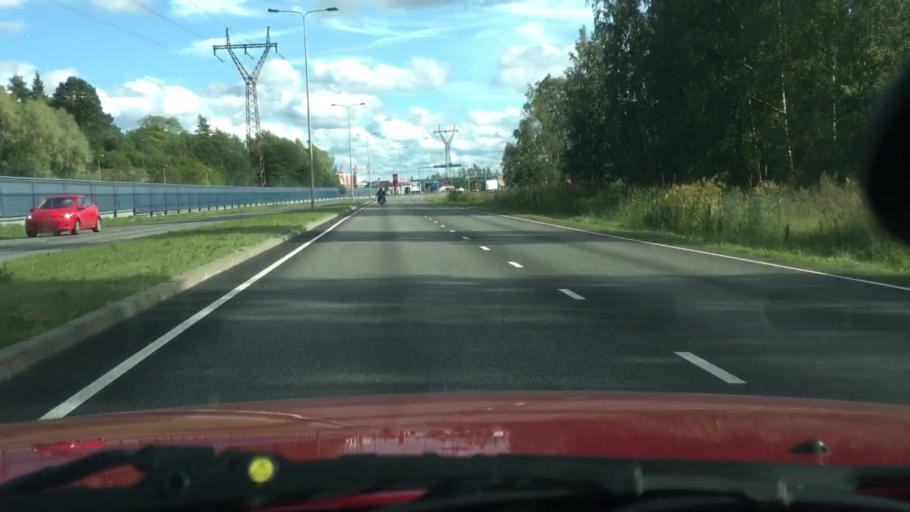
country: FI
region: Varsinais-Suomi
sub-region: Turku
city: Raisio
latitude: 60.4521
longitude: 22.1981
